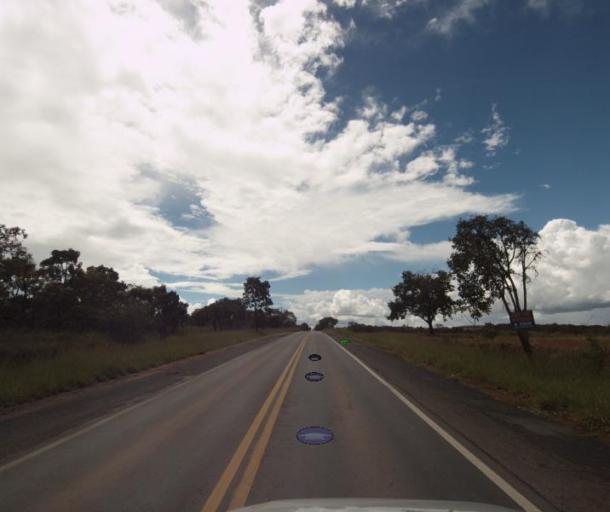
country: BR
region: Goias
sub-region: Uruacu
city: Uruacu
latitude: -14.1871
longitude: -49.1271
